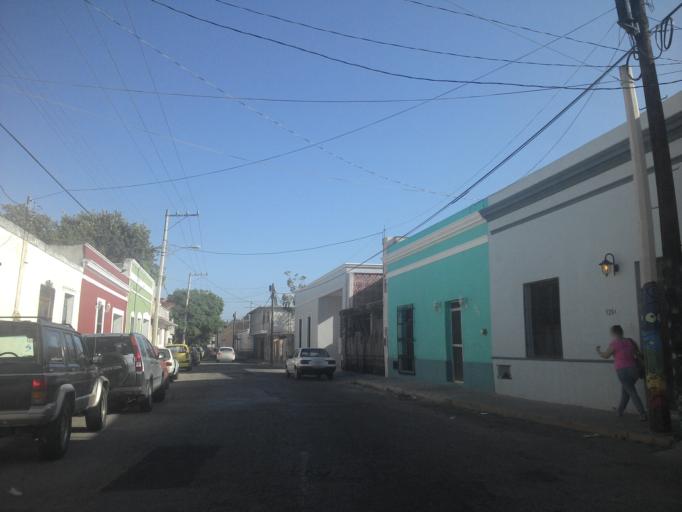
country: MX
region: Yucatan
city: Merida
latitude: 20.9659
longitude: -89.6318
